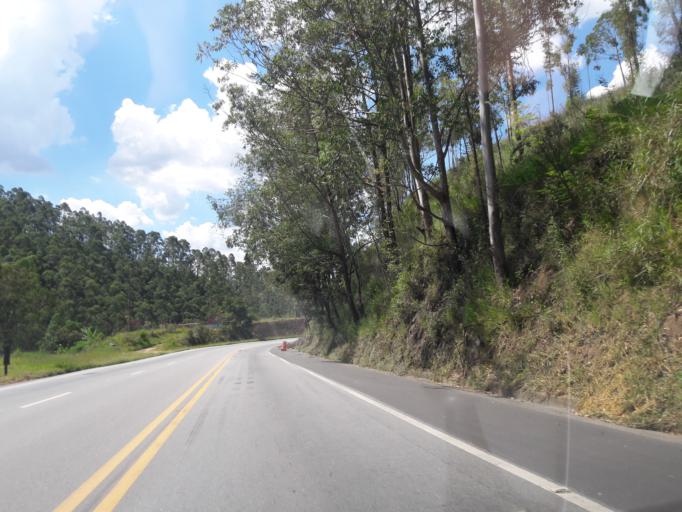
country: BR
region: Sao Paulo
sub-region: Campo Limpo Paulista
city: Campo Limpo Paulista
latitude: -23.2536
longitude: -46.7916
